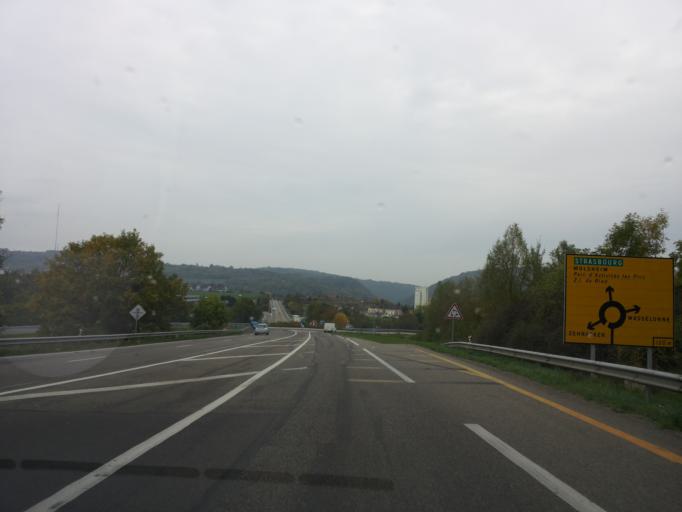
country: FR
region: Alsace
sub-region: Departement du Bas-Rhin
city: Wasselonne
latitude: 48.6456
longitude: 7.4405
